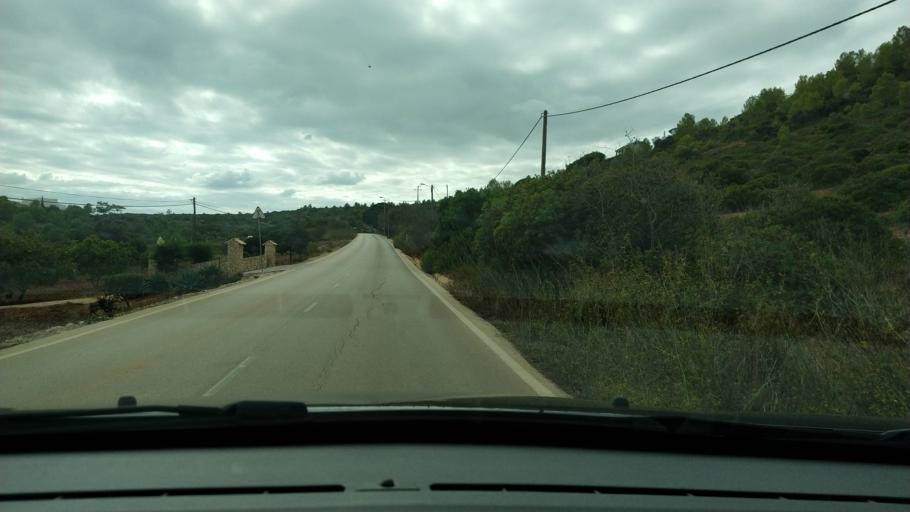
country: PT
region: Faro
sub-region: Vila do Bispo
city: Vila do Bispo
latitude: 37.0703
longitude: -8.7952
